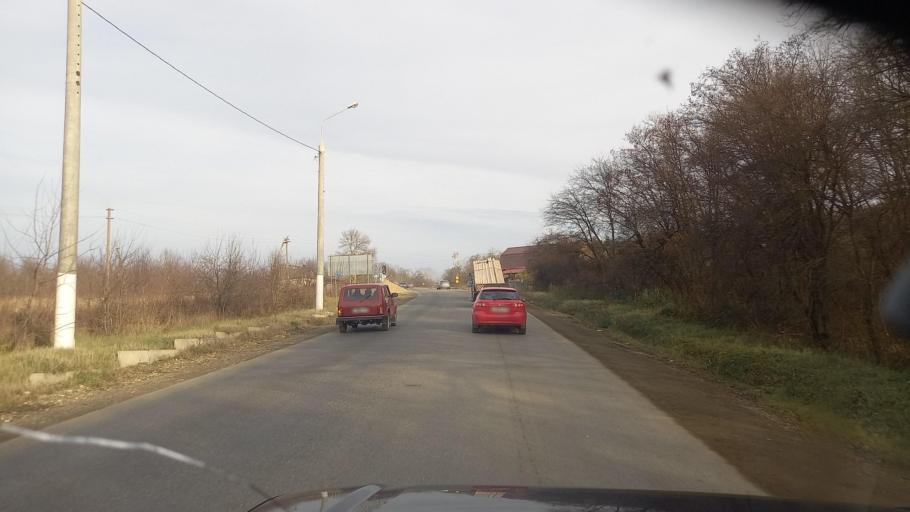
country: RU
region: Krasnodarskiy
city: Apsheronsk
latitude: 44.6039
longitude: 39.6149
